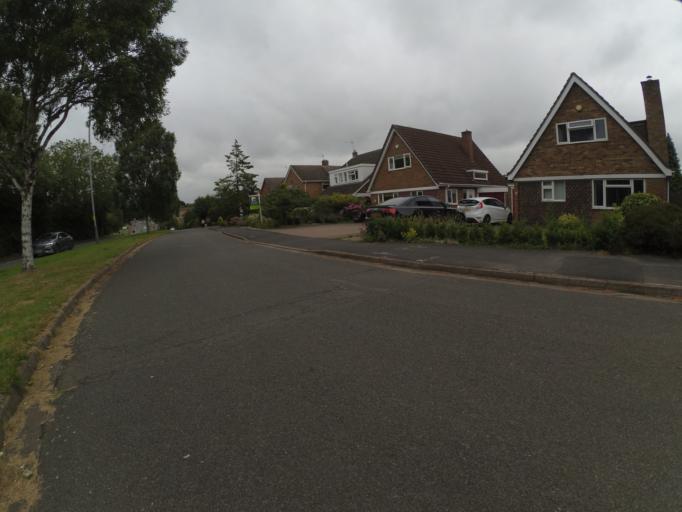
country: GB
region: England
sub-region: Warwickshire
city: Rugby
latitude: 52.3533
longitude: -1.2722
